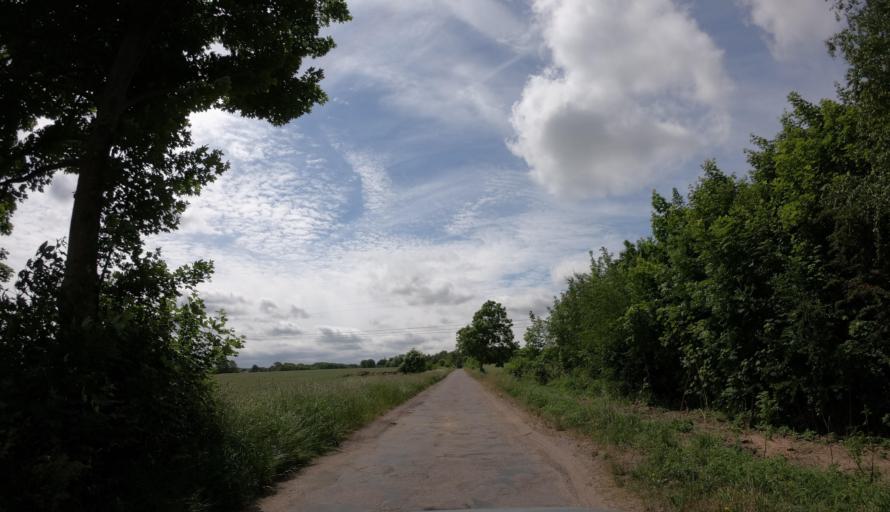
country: PL
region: West Pomeranian Voivodeship
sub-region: Powiat kamienski
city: Wolin
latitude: 53.8323
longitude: 14.7100
